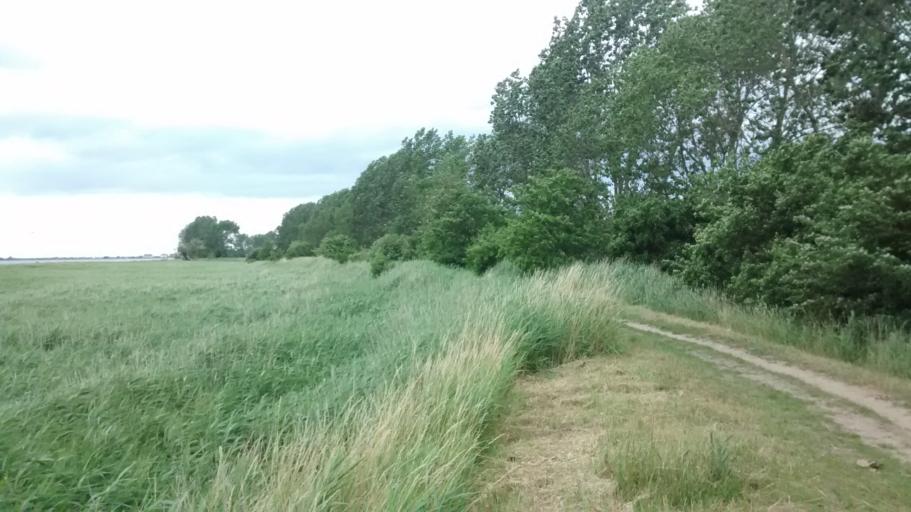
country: DE
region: Mecklenburg-Vorpommern
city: Neubukow
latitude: 54.0902
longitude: 11.6269
